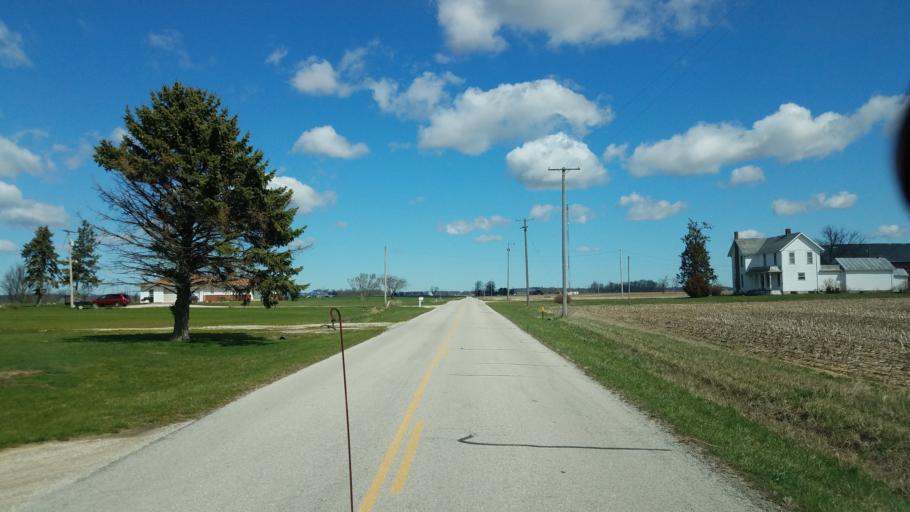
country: US
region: Ohio
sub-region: Sandusky County
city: Mount Carmel
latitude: 41.1920
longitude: -82.9376
